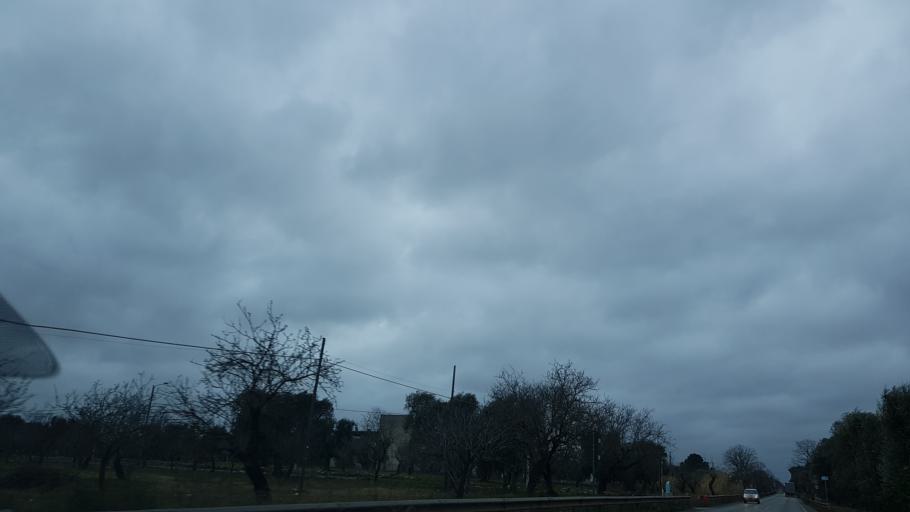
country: IT
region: Apulia
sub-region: Provincia di Brindisi
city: San Vito dei Normanni
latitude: 40.6566
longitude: 17.7354
